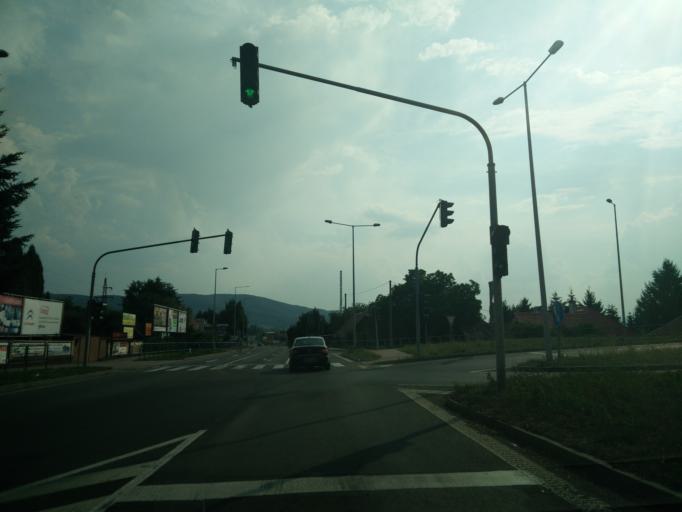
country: SK
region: Banskobystricky
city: Ziar nad Hronom
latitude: 48.5793
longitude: 18.8736
